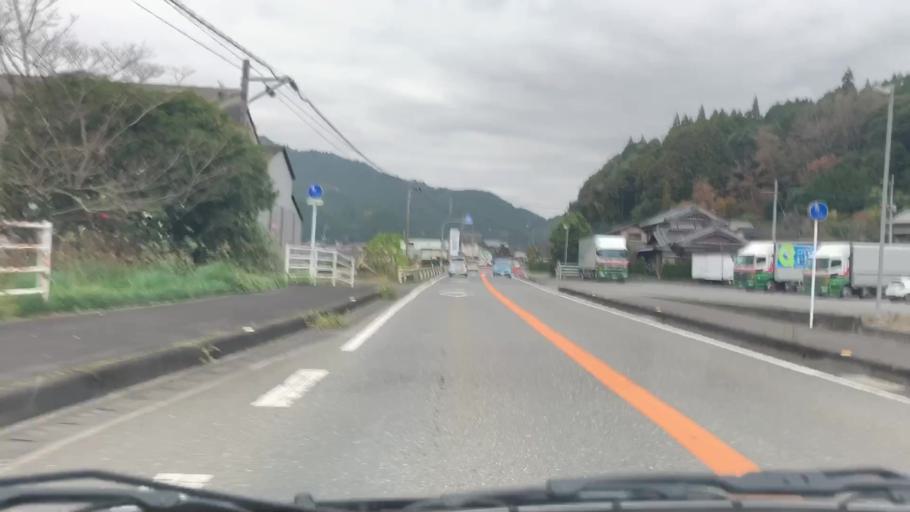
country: JP
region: Saga Prefecture
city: Ureshinomachi-shimojuku
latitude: 33.1270
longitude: 130.0394
